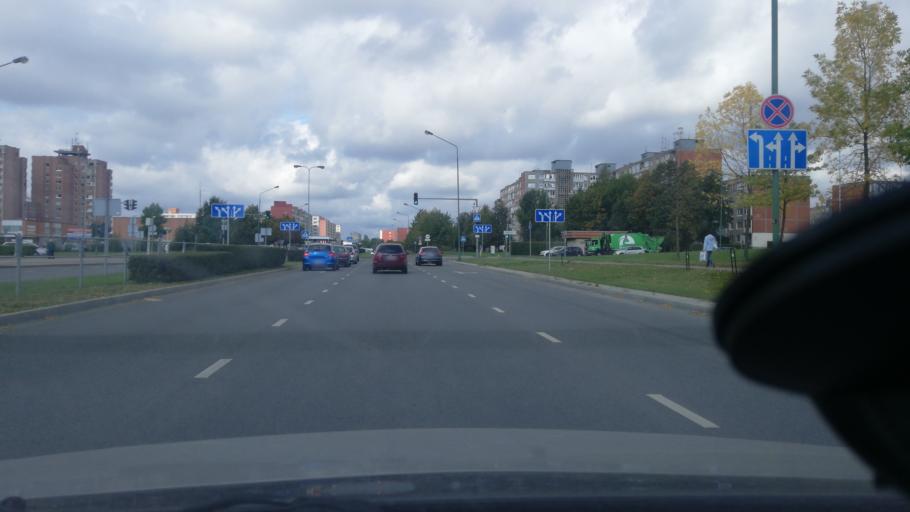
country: LT
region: Klaipedos apskritis
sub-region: Klaipeda
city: Klaipeda
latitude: 55.6699
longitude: 21.1938
